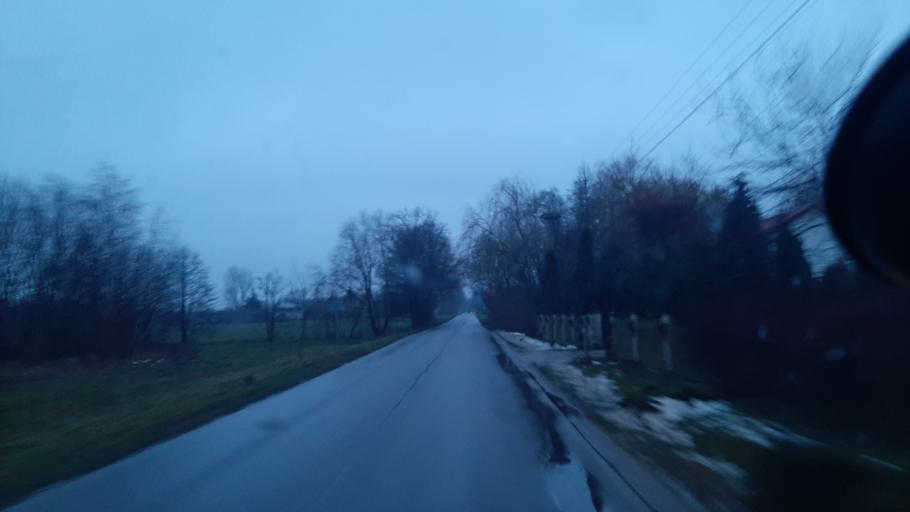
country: PL
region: Lublin Voivodeship
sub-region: Powiat lubelski
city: Garbow
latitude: 51.3934
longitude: 22.4096
